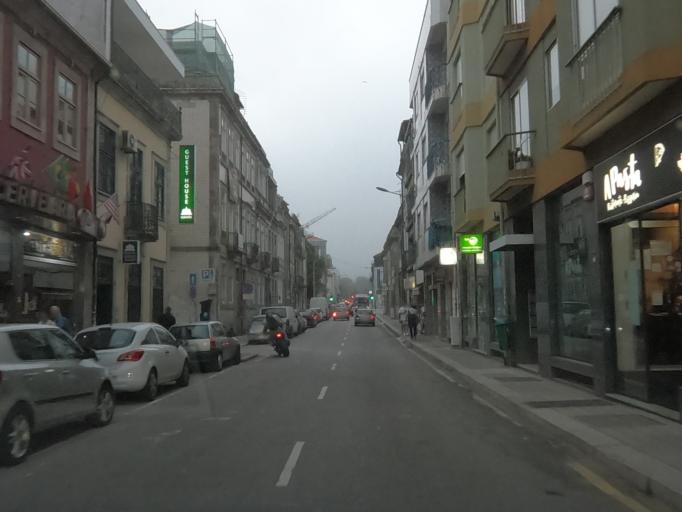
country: PT
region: Porto
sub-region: Porto
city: Porto
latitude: 41.1566
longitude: -8.6210
